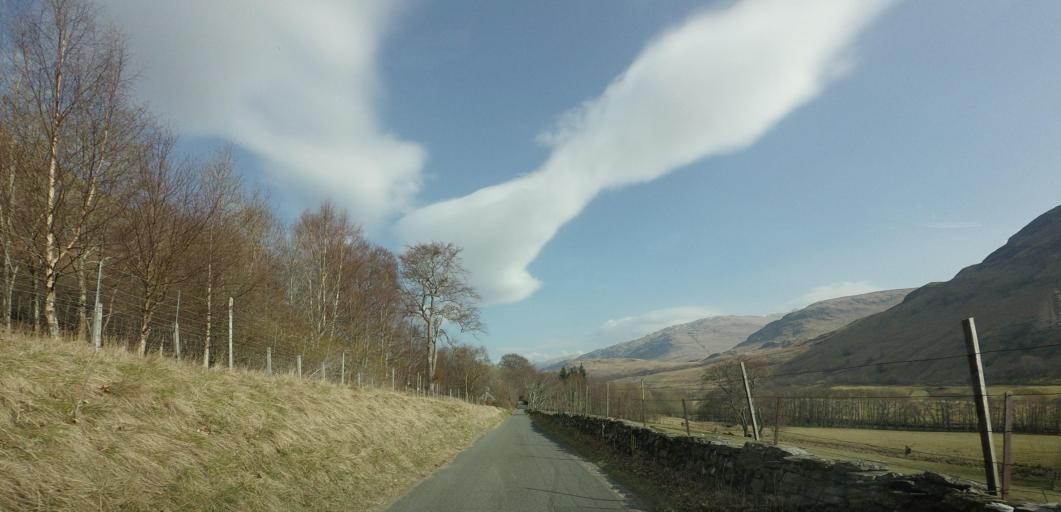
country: GB
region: Scotland
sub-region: Stirling
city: Callander
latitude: 56.5988
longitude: -4.2852
